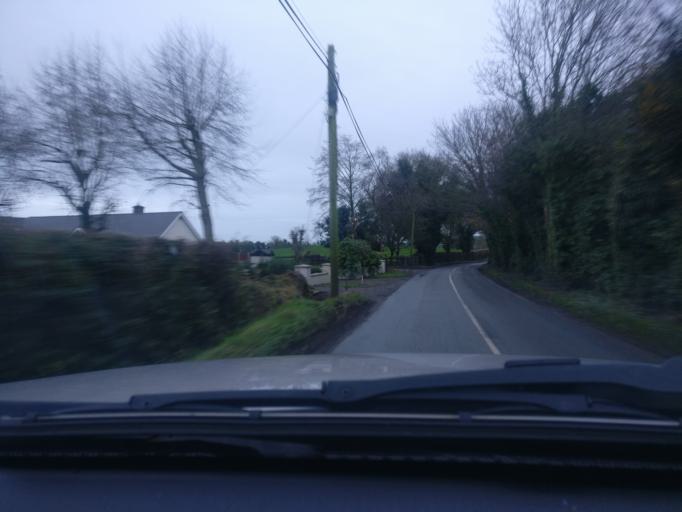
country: IE
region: Leinster
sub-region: An Mhi
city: Dunshaughlin
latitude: 53.4994
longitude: -6.6004
